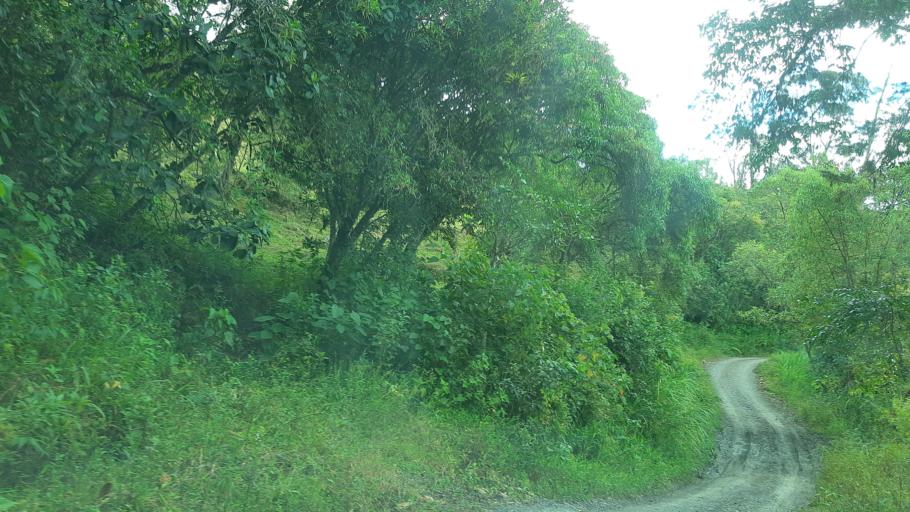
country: CO
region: Boyaca
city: Garagoa
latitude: 5.0242
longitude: -73.3271
